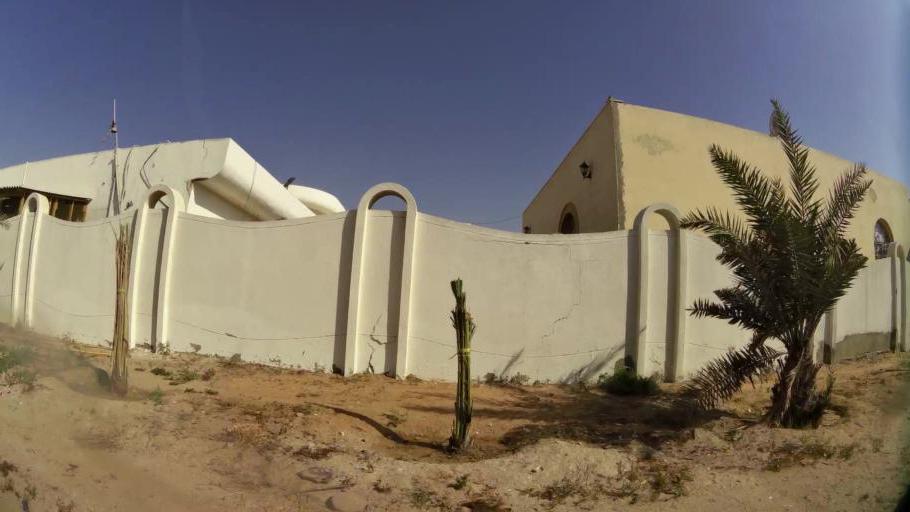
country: AE
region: Ajman
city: Ajman
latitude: 25.4193
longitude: 55.4633
